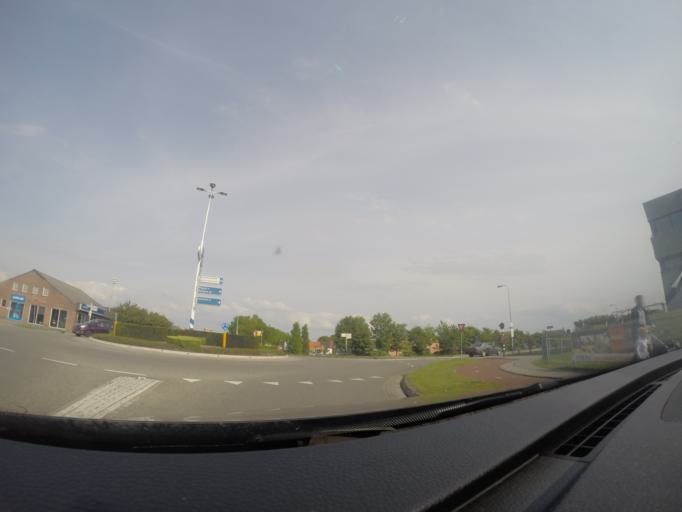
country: NL
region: Flevoland
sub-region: Gemeente Urk
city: Urk
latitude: 52.6607
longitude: 5.6029
